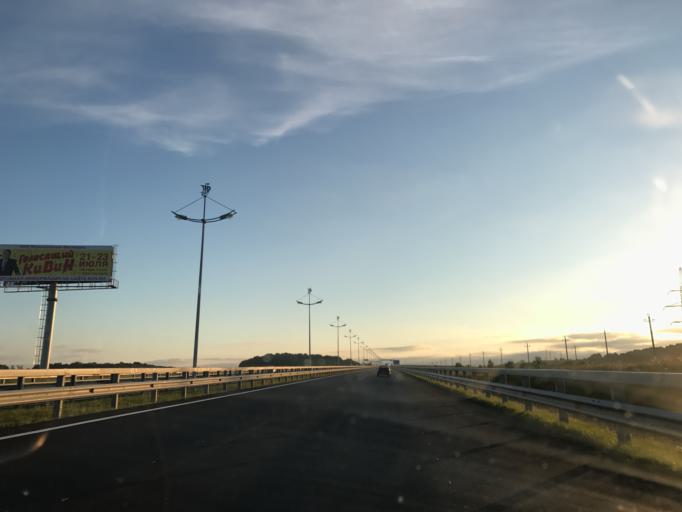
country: RU
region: Kaliningrad
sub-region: Gorod Kaliningrad
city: Pionerskiy
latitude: 54.9207
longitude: 20.2848
